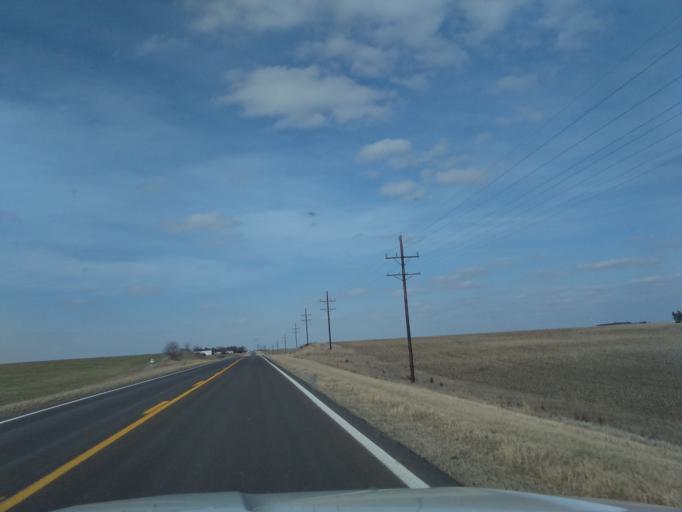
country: US
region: Nebraska
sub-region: Gage County
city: Beatrice
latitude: 40.1619
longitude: -96.9351
